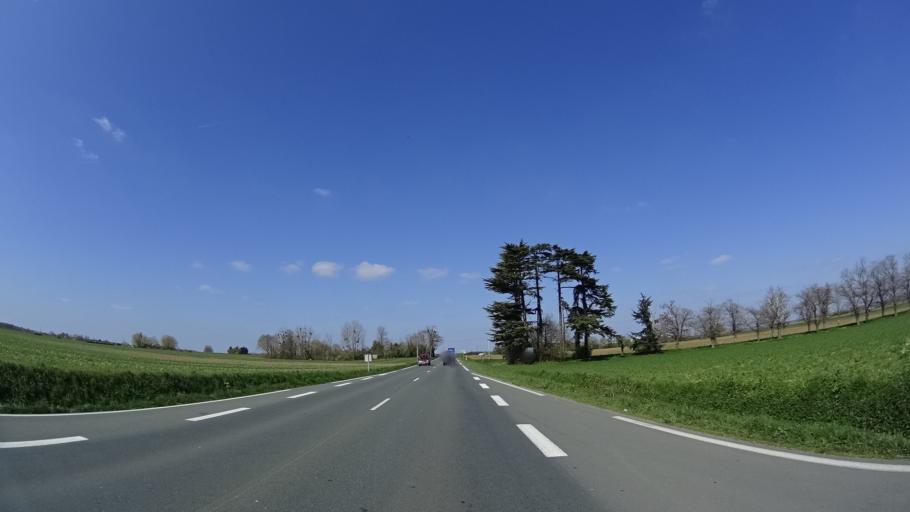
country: FR
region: Pays de la Loire
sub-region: Departement de Maine-et-Loire
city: Brissac-Quince
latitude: 47.3322
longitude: -0.4237
